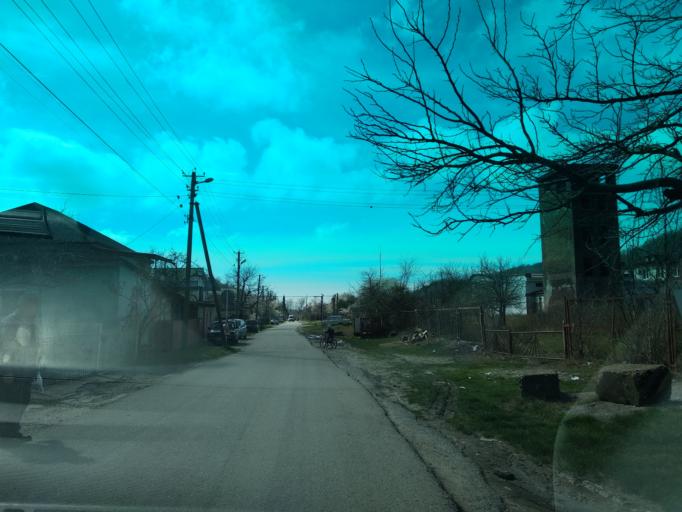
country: RU
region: Krasnodarskiy
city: Shepsi
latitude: 44.0515
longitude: 39.1615
